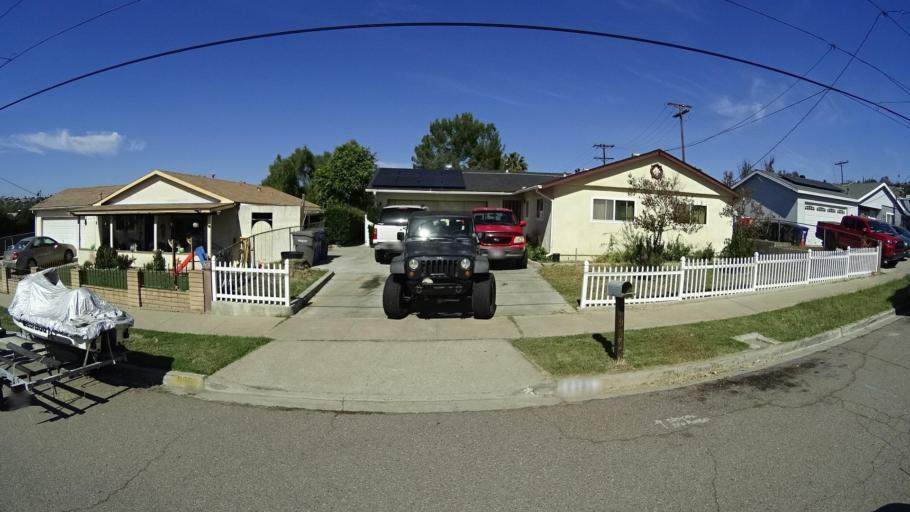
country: US
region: California
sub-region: San Diego County
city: Spring Valley
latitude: 32.7286
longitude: -117.0068
